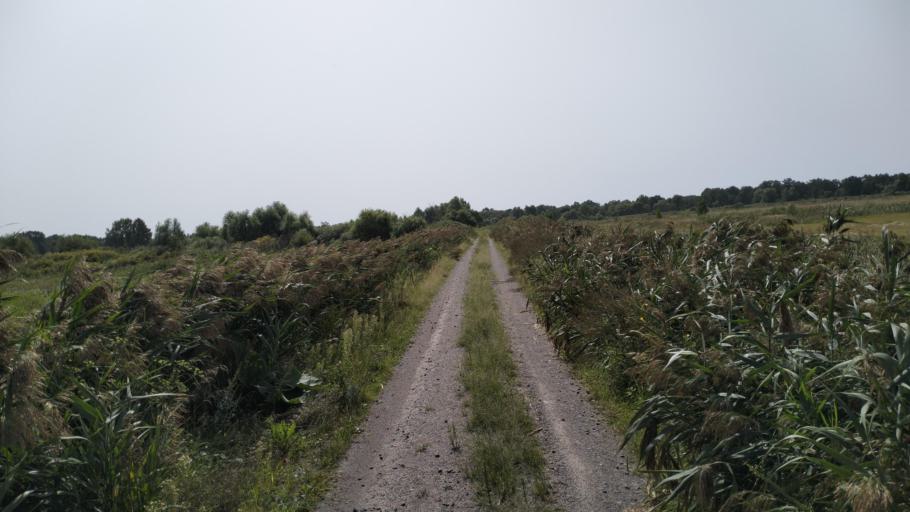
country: BY
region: Brest
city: Davyd-Haradok
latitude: 51.9694
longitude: 27.1736
